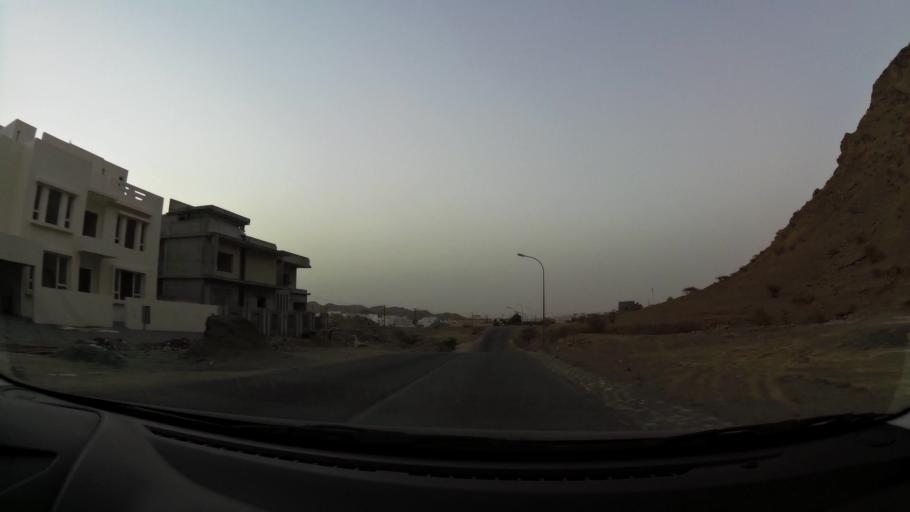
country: OM
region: Muhafazat Masqat
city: Bawshar
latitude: 23.4973
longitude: 58.3445
